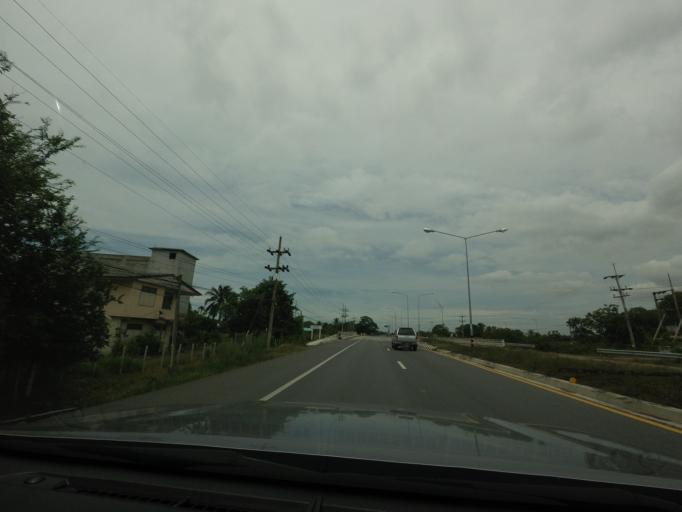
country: TH
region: Nakhon Si Thammarat
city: Hua Sai
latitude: 7.9129
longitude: 100.3377
